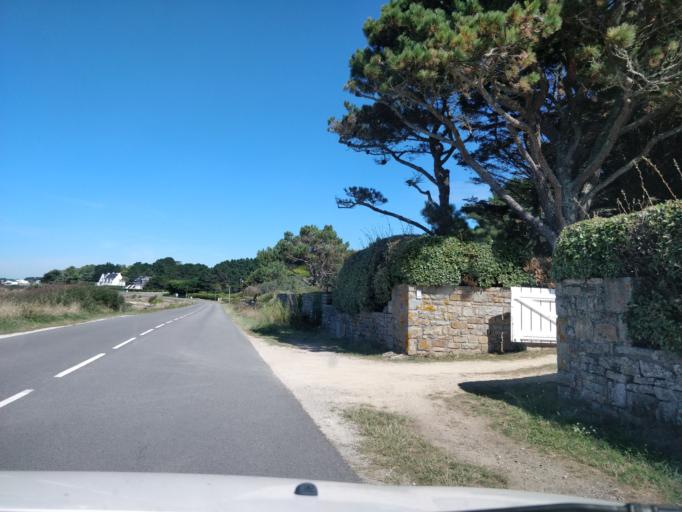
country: FR
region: Brittany
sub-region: Departement du Morbihan
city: Saint-Philibert
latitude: 47.5696
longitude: -3.0072
